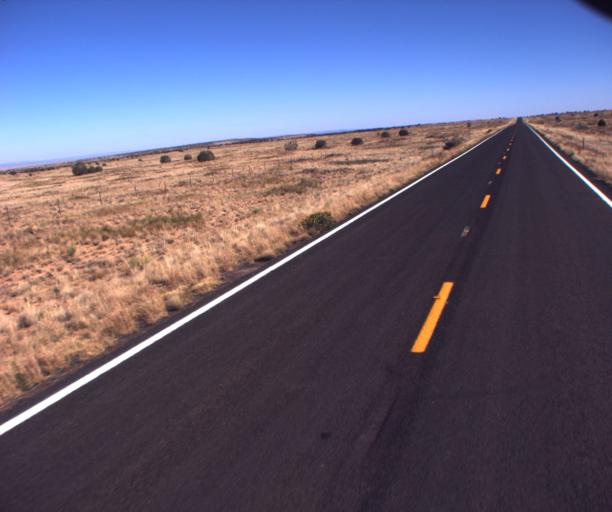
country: US
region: Arizona
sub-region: Coconino County
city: Tuba City
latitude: 35.9090
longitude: -110.8748
